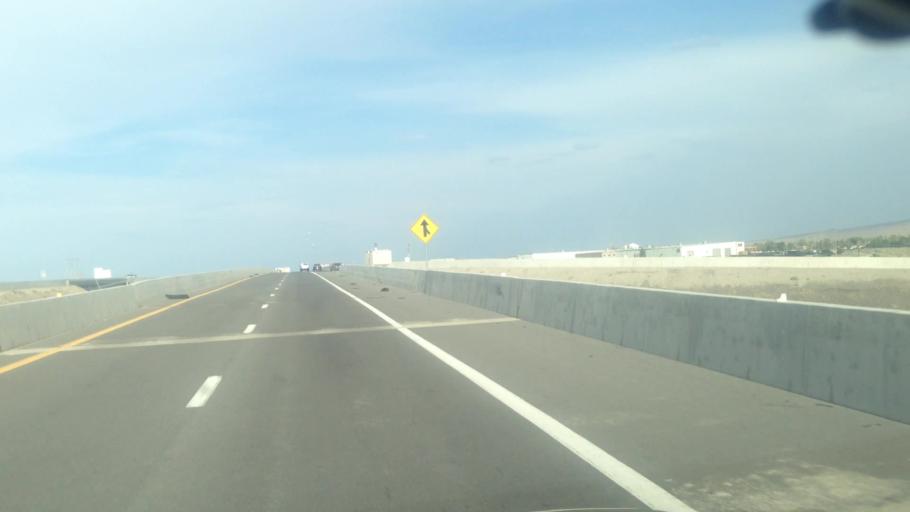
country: US
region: Nevada
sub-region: Lyon County
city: Fernley
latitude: 39.6159
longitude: -119.2654
